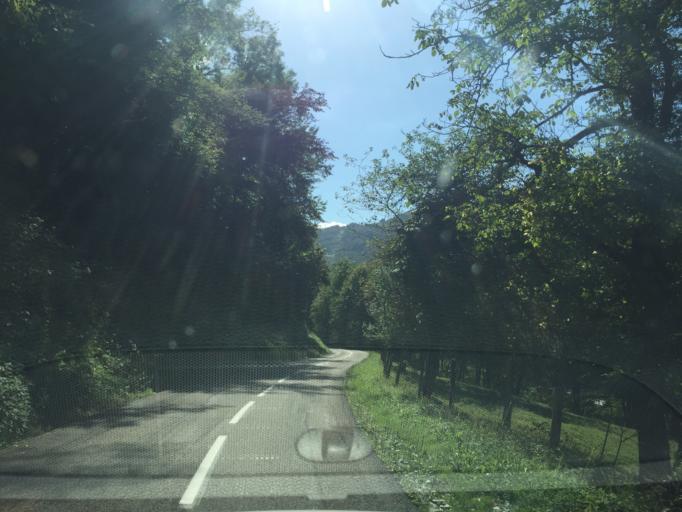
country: FR
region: Rhone-Alpes
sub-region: Departement de la Savoie
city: Coise-Saint-Jean-Pied-Gauthier
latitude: 45.4856
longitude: 6.1540
